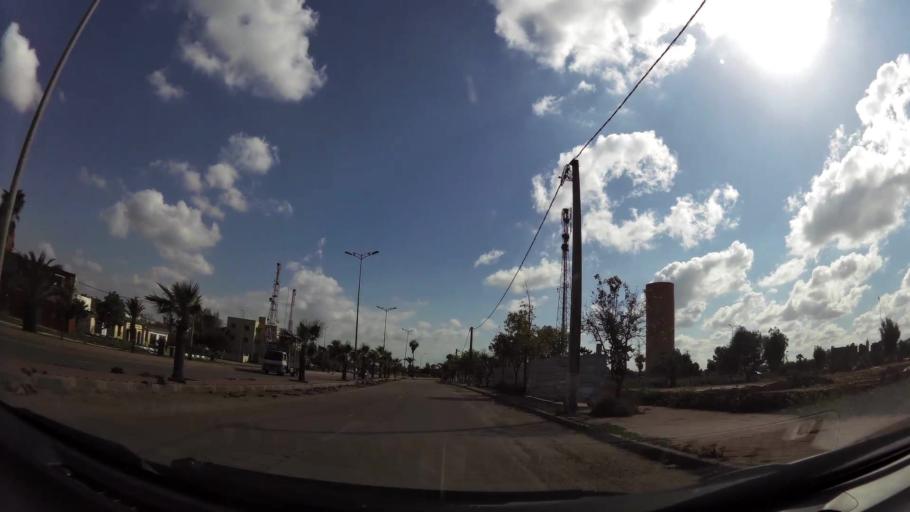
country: MA
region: Grand Casablanca
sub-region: Mediouna
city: Mediouna
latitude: 33.4569
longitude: -7.5211
